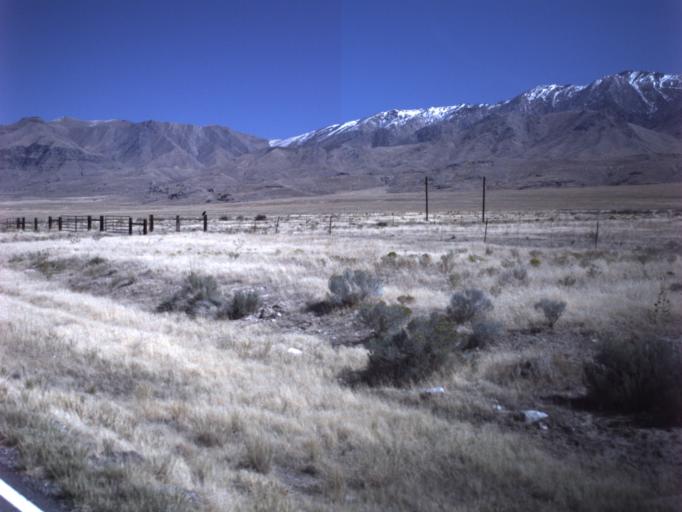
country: US
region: Utah
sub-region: Tooele County
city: Grantsville
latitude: 40.5947
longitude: -112.7177
